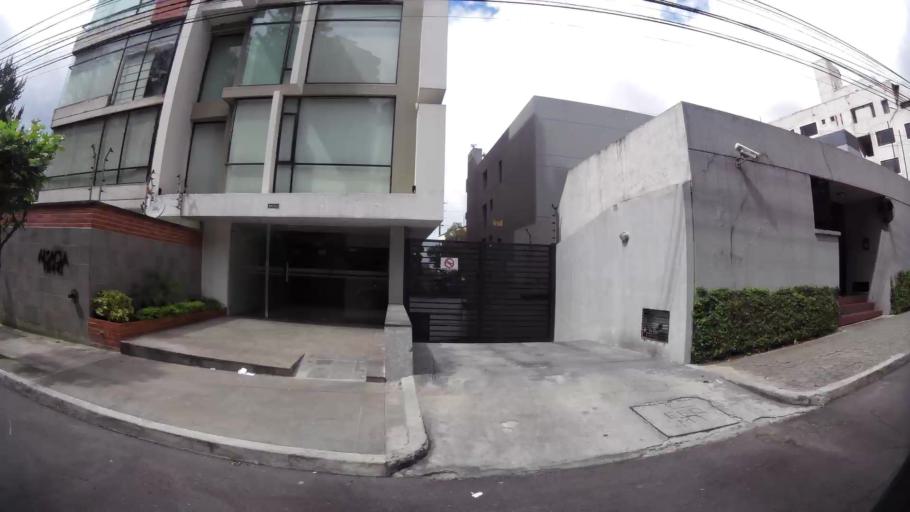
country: EC
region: Pichincha
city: Quito
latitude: -0.1643
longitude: -78.4950
